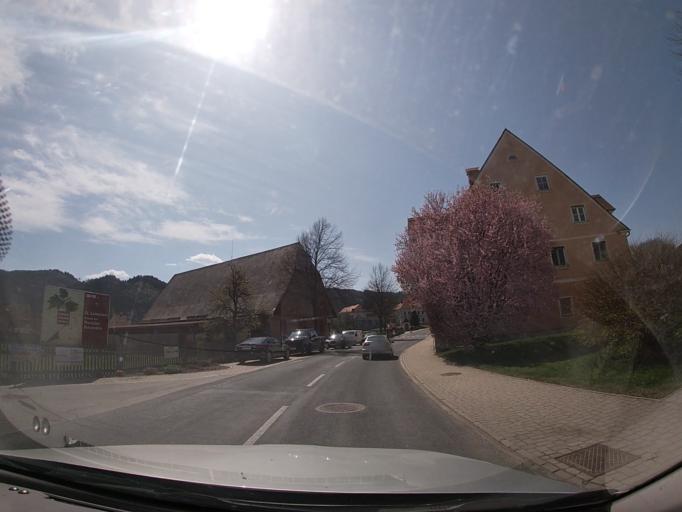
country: AT
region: Styria
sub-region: Politischer Bezirk Murtal
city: Sankt Lorenzen bei Knittelfeld
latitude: 47.2509
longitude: 14.8961
